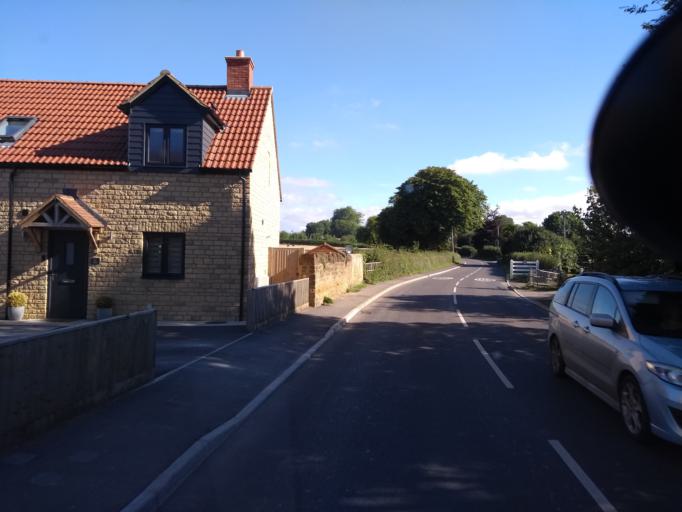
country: GB
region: England
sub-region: Somerset
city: Martock
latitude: 50.9811
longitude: -2.7660
